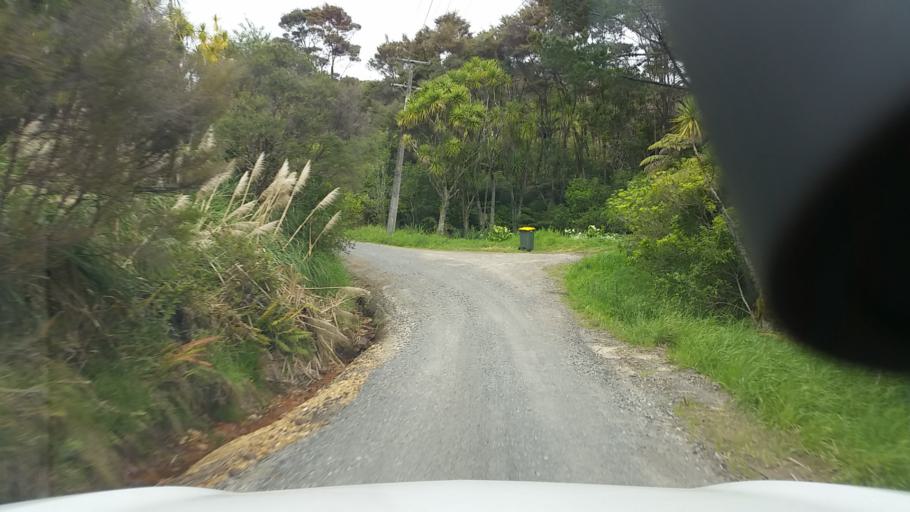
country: NZ
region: Auckland
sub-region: Auckland
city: Muriwai Beach
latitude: -36.8753
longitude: 174.5096
